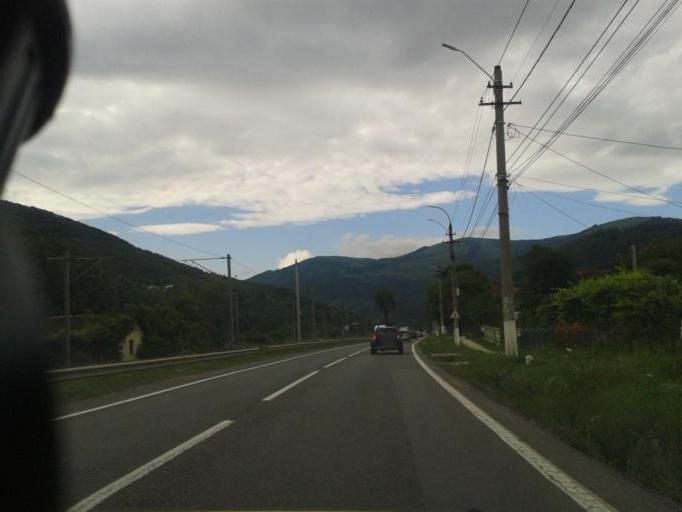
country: RO
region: Prahova
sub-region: Comuna Comarnic
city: Comarnic
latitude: 45.2611
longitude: 25.6248
